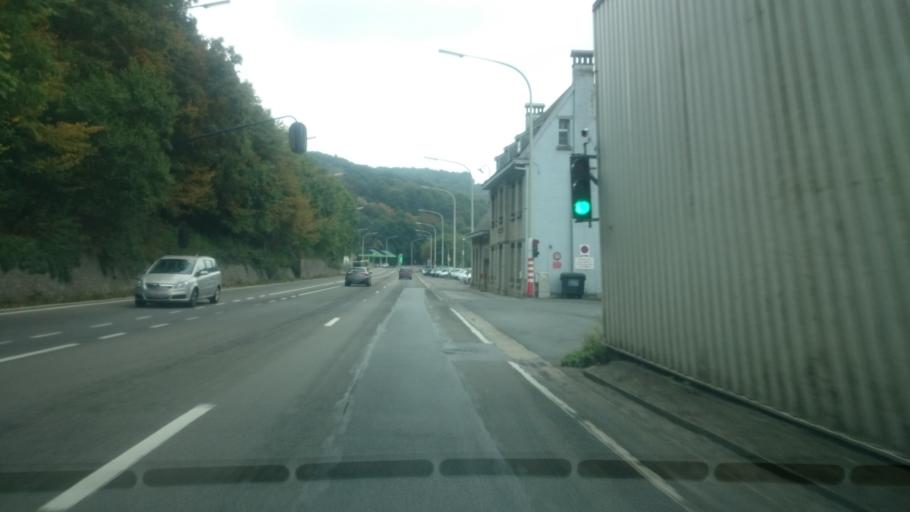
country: BE
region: Wallonia
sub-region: Province de Namur
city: Namur
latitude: 50.4530
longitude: 4.8350
